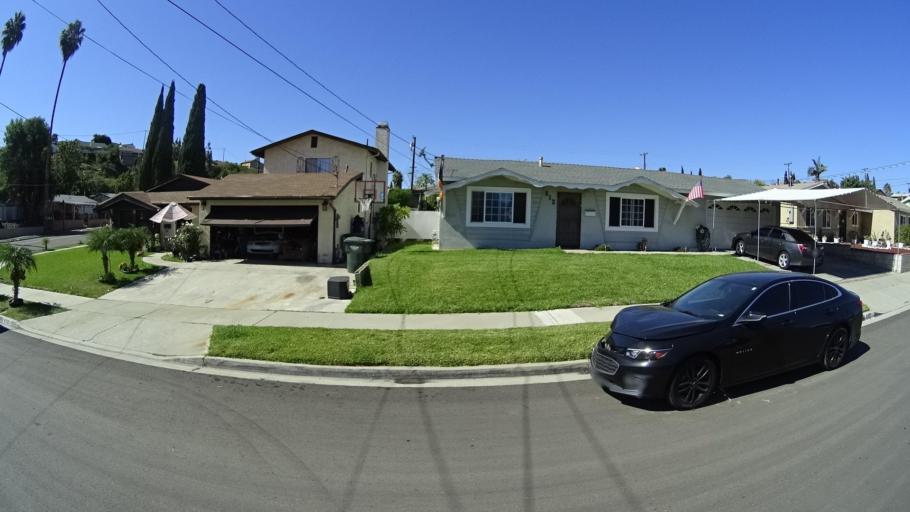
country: US
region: California
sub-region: San Diego County
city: La Presa
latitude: 32.7019
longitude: -117.0188
